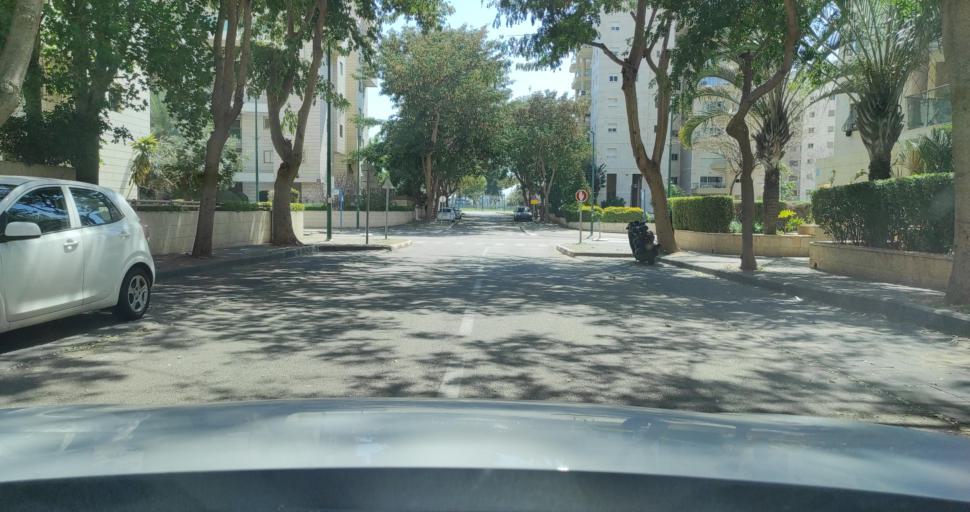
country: IL
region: Central District
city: Nordiyya
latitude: 32.2982
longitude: 34.8714
